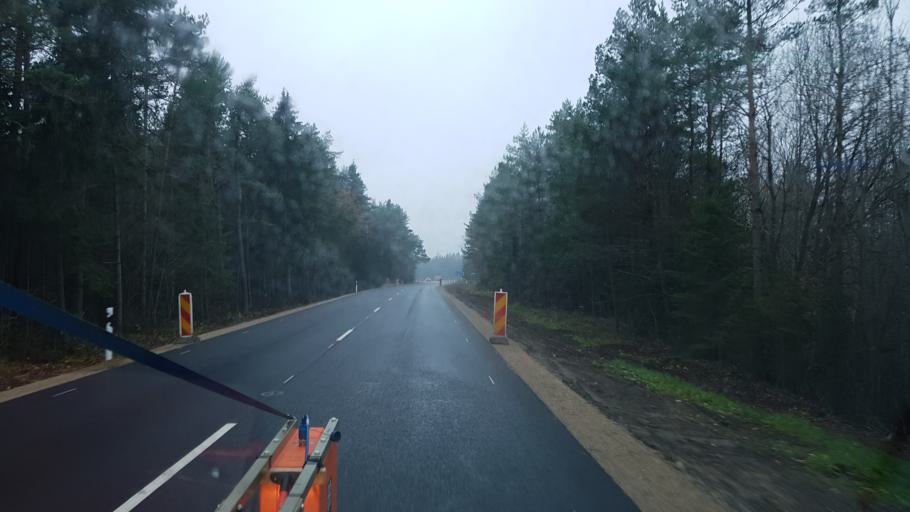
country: EE
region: Raplamaa
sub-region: Kohila vald
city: Kohila
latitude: 59.1788
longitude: 24.7872
